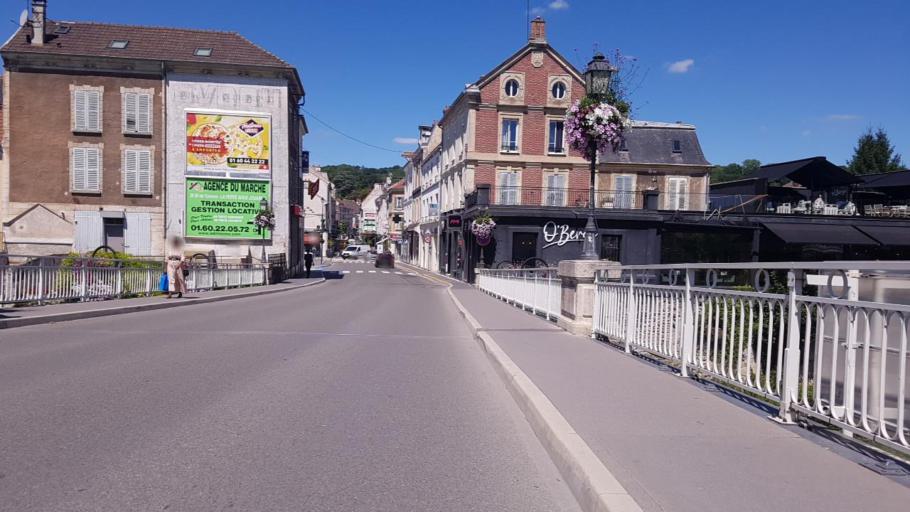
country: FR
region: Ile-de-France
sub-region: Departement de Seine-et-Marne
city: La Ferte-sous-Jouarre
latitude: 48.9488
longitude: 3.1319
